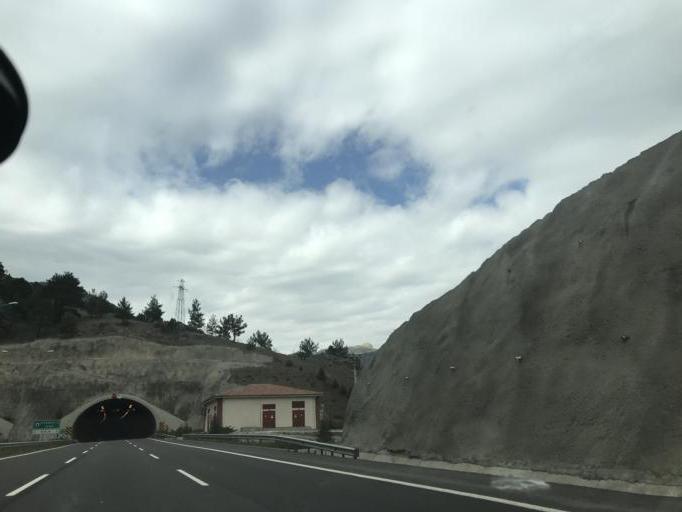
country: TR
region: Nigde
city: Ciftehan
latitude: 37.5205
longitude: 34.8177
